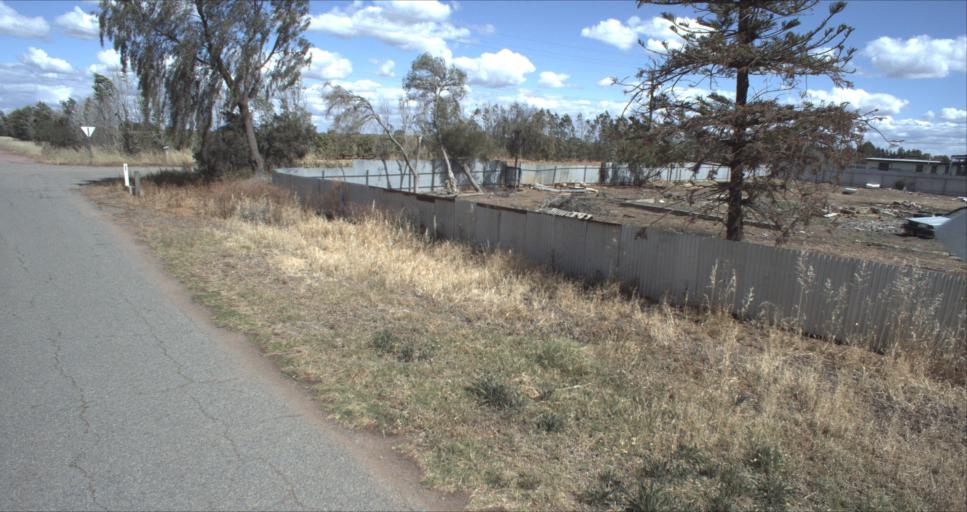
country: AU
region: New South Wales
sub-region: Leeton
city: Leeton
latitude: -34.5174
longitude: 146.2349
